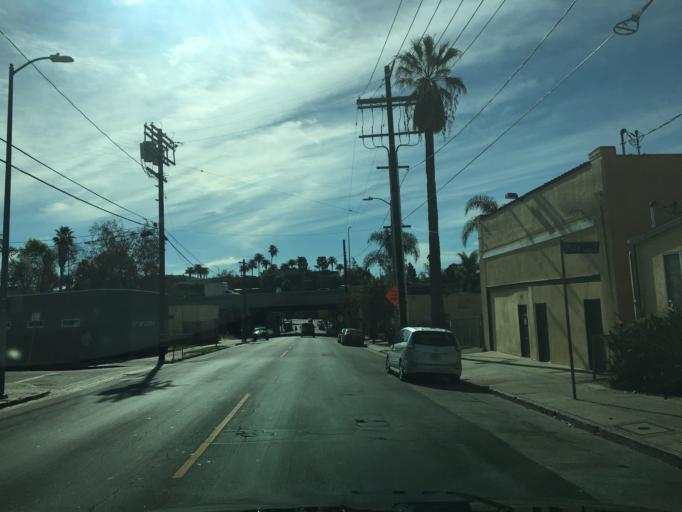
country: US
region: California
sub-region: Los Angeles County
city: Silver Lake
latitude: 34.0790
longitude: -118.2845
